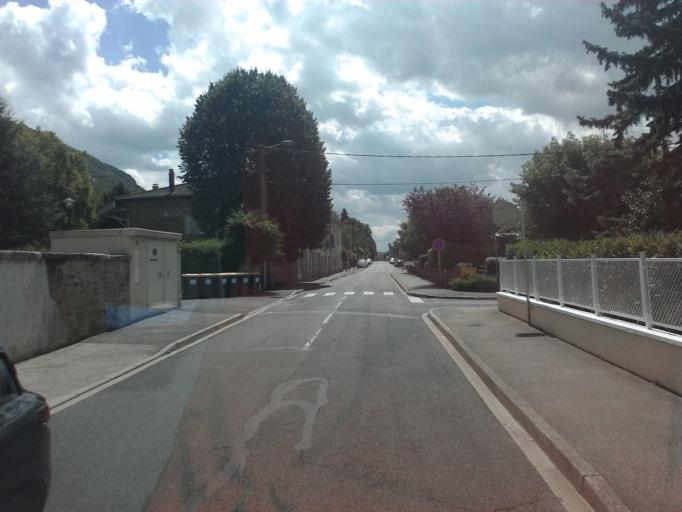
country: FR
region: Rhone-Alpes
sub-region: Departement de l'Ain
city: Lagnieu
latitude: 45.9010
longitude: 5.3513
